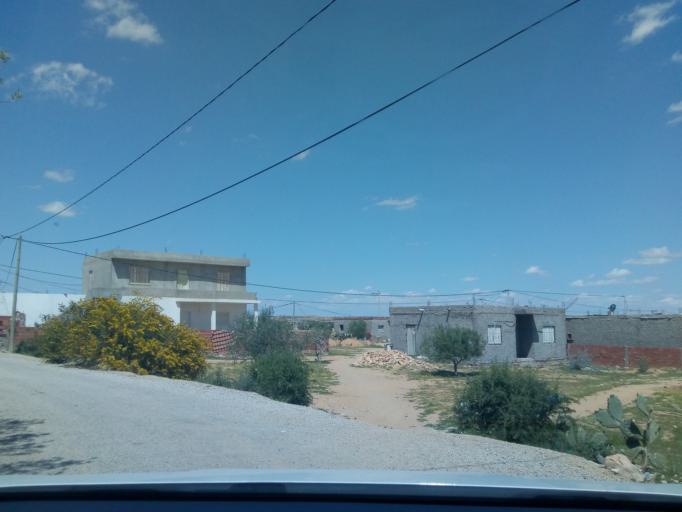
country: TN
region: Safaqis
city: Sfax
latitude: 34.7312
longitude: 10.4921
